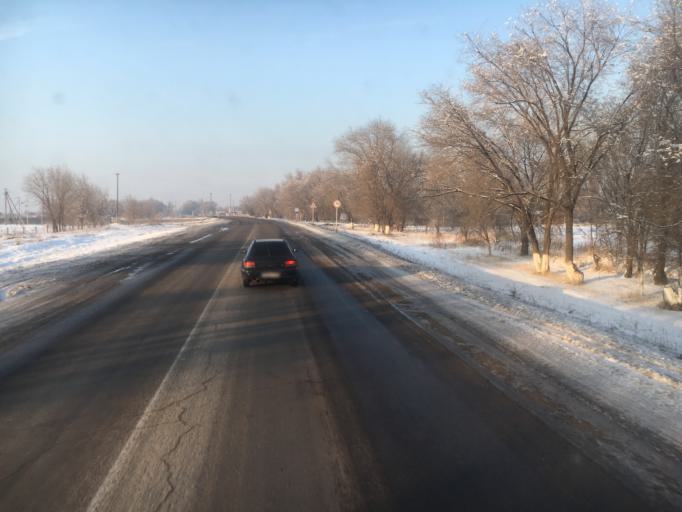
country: KZ
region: Almaty Oblysy
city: Burunday
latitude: 43.3299
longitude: 76.6621
